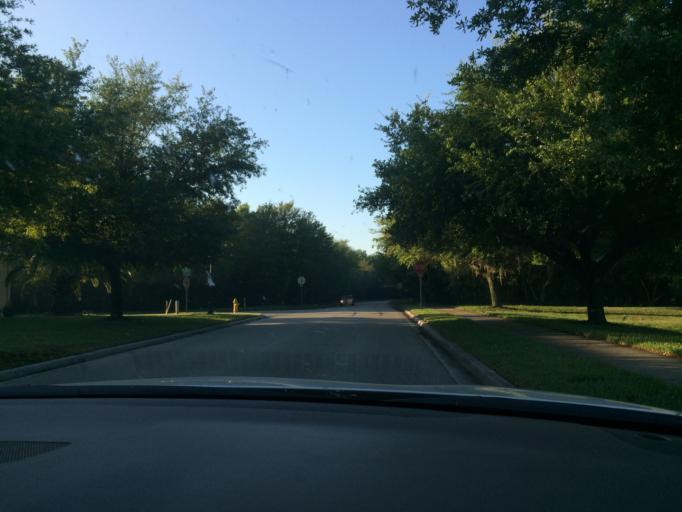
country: US
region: Florida
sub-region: Manatee County
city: Ellenton
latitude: 27.4931
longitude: -82.4113
